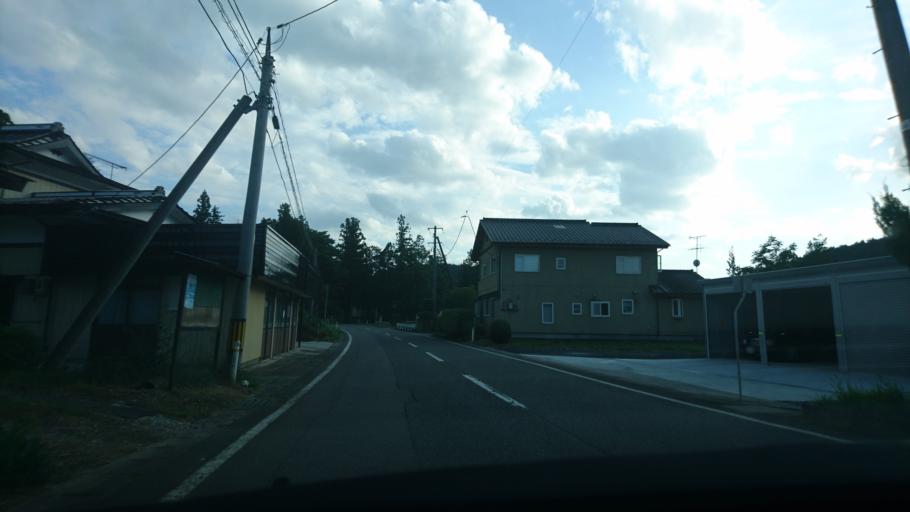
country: JP
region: Iwate
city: Ichinoseki
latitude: 39.0199
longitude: 141.2899
